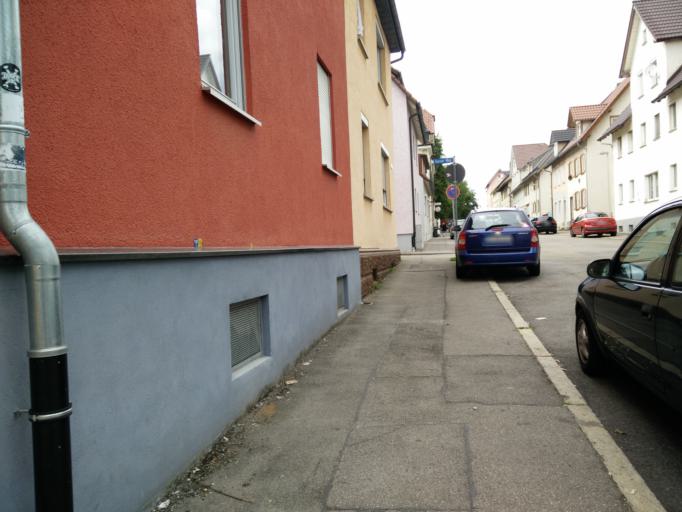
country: DE
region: Baden-Wuerttemberg
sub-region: Freiburg Region
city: Dauchingen
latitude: 48.0600
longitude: 8.5315
